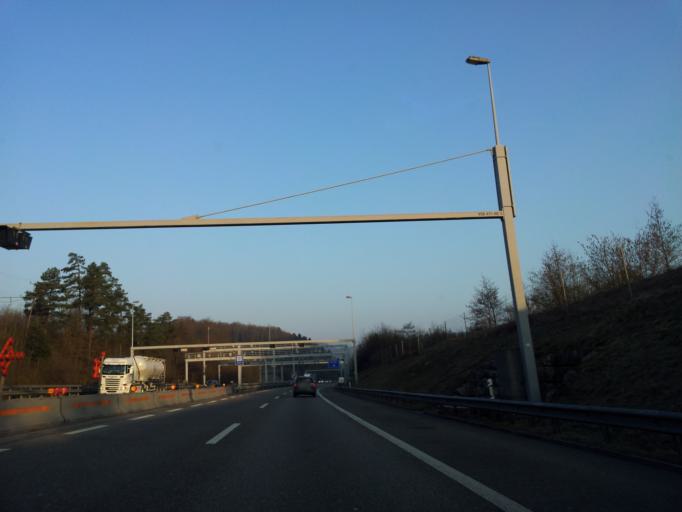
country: CH
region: Aargau
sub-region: Bezirk Brugg
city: Schinznach Dorf
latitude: 47.4786
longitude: 8.1002
